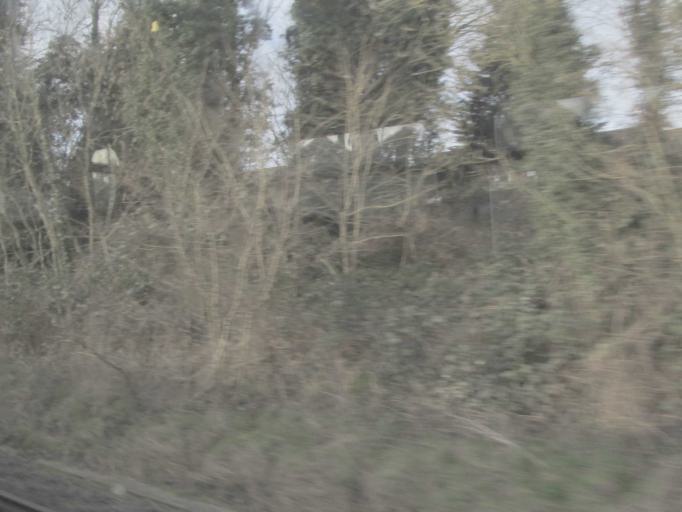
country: GB
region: England
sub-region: Wokingham
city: Earley
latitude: 51.4491
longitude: -0.9323
